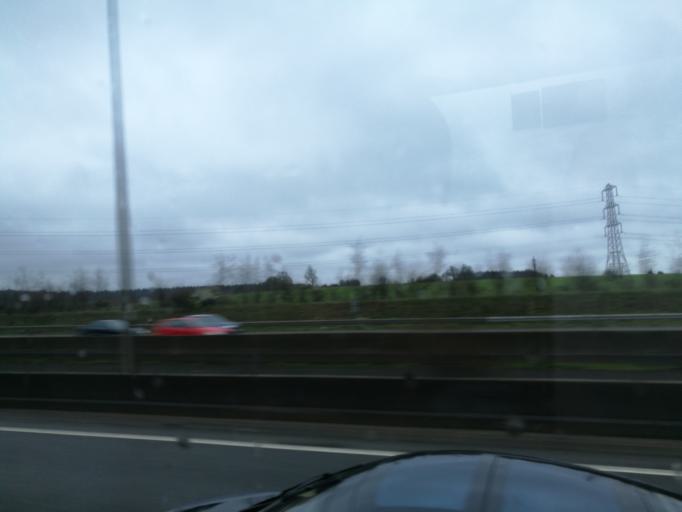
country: GB
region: England
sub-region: Hertfordshire
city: Abbots Langley
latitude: 51.7313
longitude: -0.3914
